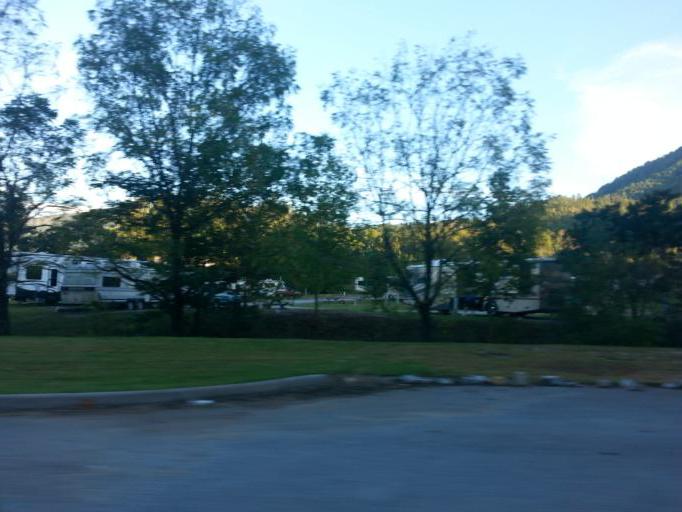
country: US
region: Tennessee
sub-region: Sevier County
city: Pigeon Forge
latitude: 35.7055
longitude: -83.6712
